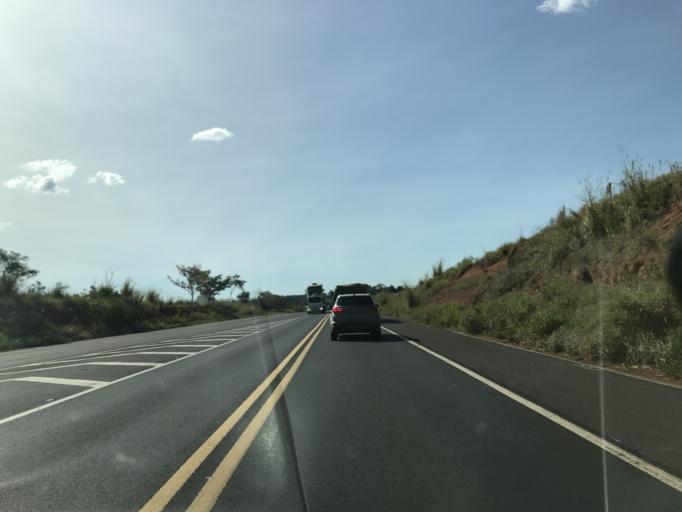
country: BR
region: Sao Paulo
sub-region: Pirapozinho
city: Pirapozinho
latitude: -22.4838
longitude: -51.6633
